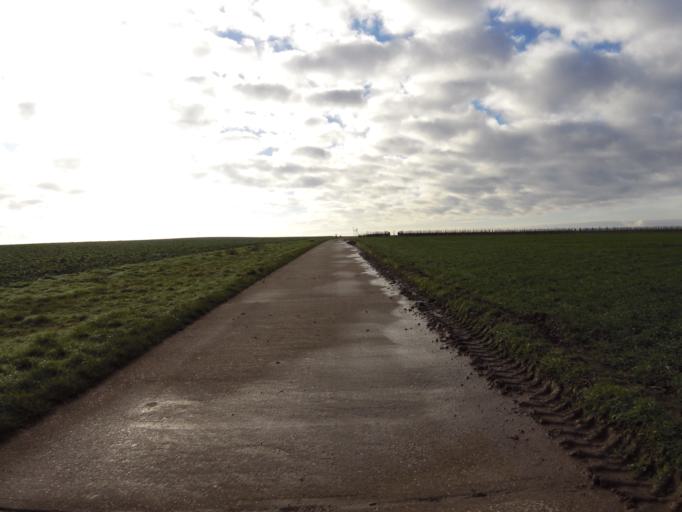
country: DE
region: Rheinland-Pfalz
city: Obrigheim
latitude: 49.5850
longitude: 8.2127
